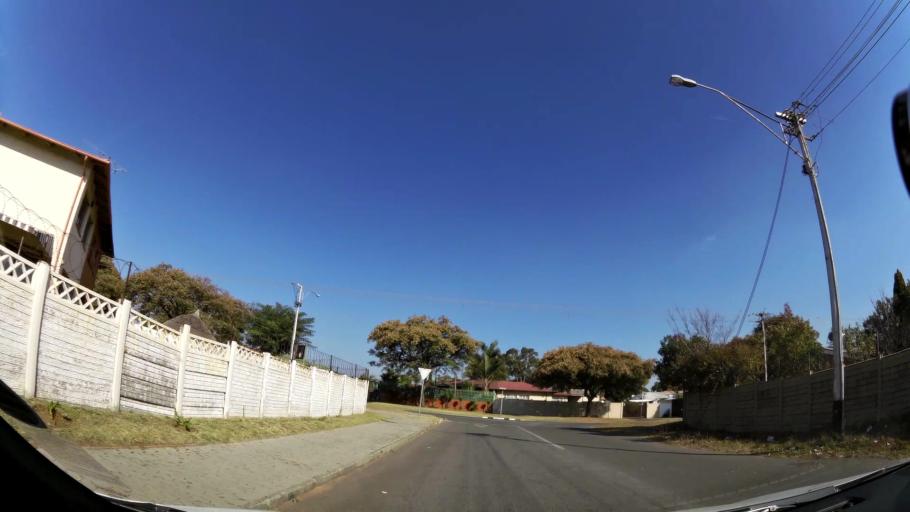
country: ZA
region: Gauteng
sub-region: City of Johannesburg Metropolitan Municipality
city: Johannesburg
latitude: -26.2518
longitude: 28.0040
